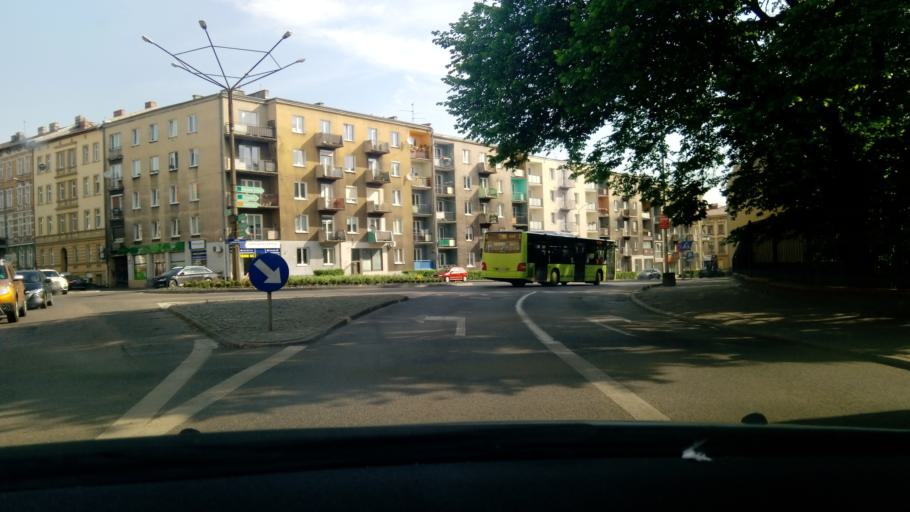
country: PL
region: Lubusz
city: Gorzow Wielkopolski
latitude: 52.7326
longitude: 15.2318
